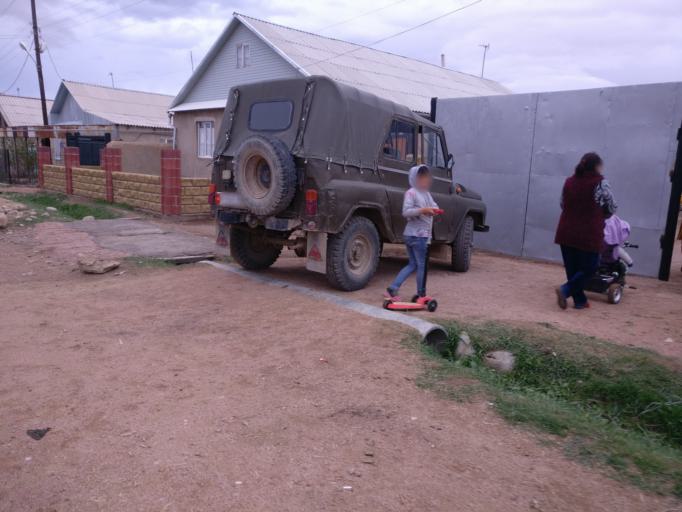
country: KG
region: Ysyk-Koel
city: Bokombayevskoye
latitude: 42.1096
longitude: 76.9809
